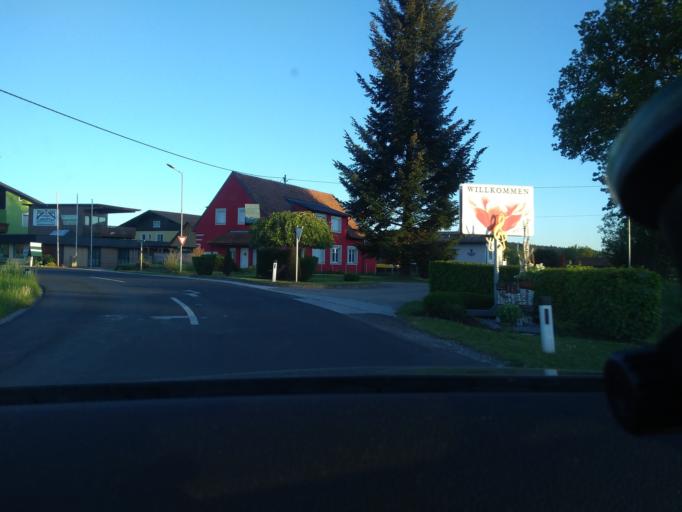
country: AT
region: Styria
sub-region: Politischer Bezirk Voitsberg
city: Mooskirchen
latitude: 46.9905
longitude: 15.2804
